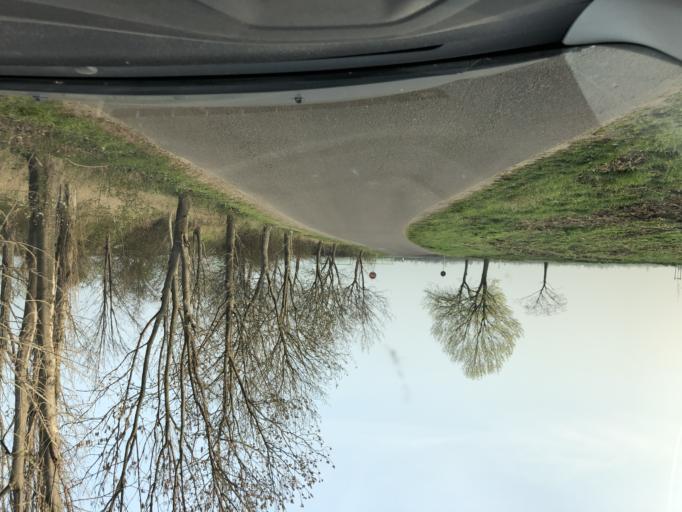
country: DE
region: Saxony-Anhalt
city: Brehna
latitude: 51.5638
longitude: 12.2183
